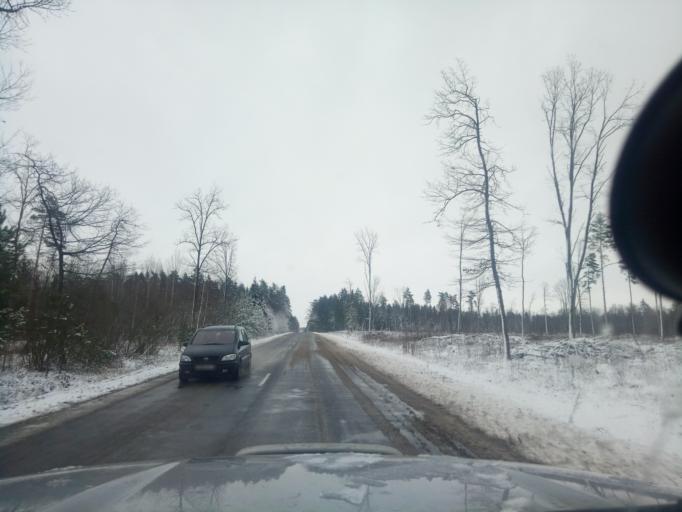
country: BY
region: Minsk
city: Tsimkavichy
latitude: 53.0510
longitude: 26.8794
